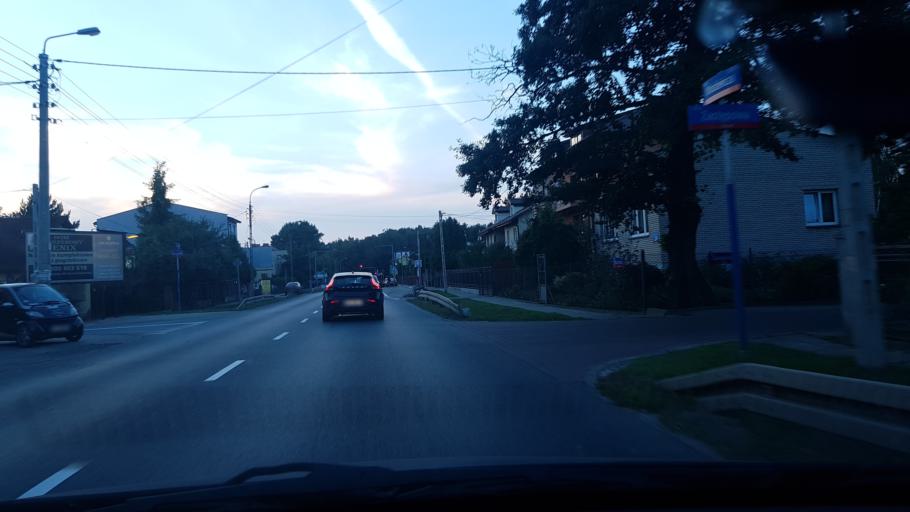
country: PL
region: Masovian Voivodeship
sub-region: Warszawa
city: Targowek
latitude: 52.2897
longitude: 21.0714
